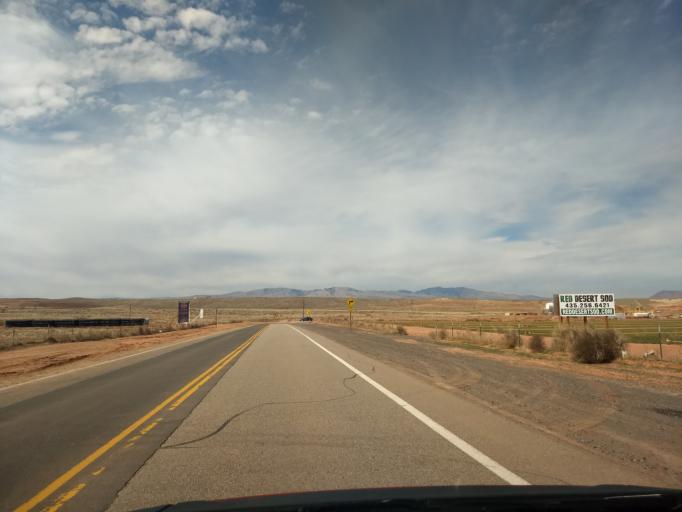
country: US
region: Utah
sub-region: Washington County
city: Washington
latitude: 37.0592
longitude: -113.4883
